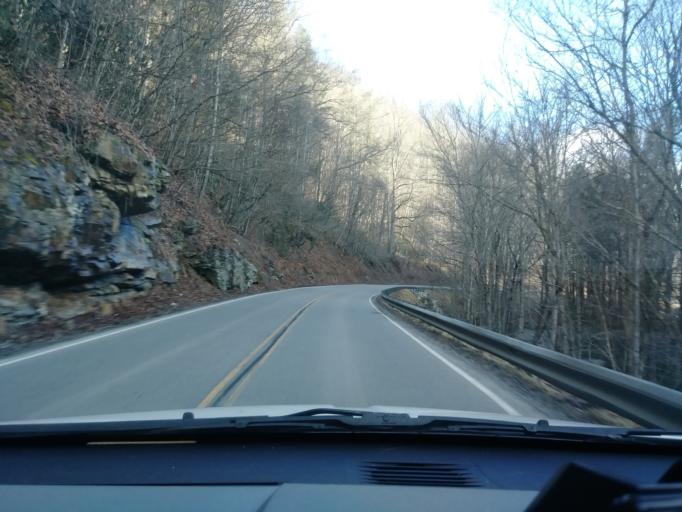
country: US
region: North Carolina
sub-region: Avery County
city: Newland
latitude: 36.1606
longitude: -81.9612
